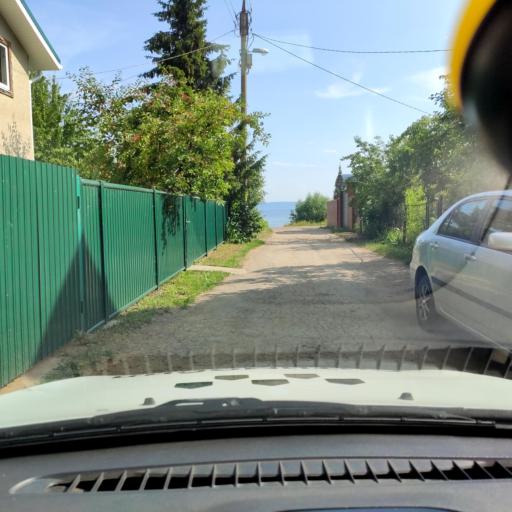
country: RU
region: Samara
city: Podstepki
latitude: 53.5032
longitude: 49.1441
